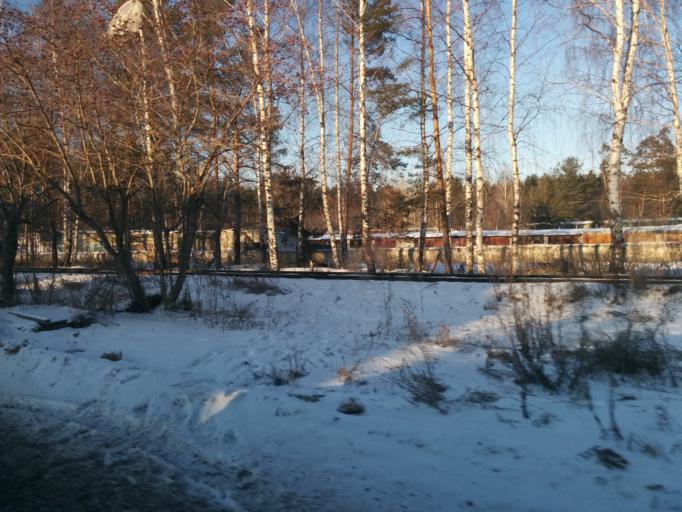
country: RU
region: Perm
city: Overyata
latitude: 58.0167
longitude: 55.9643
